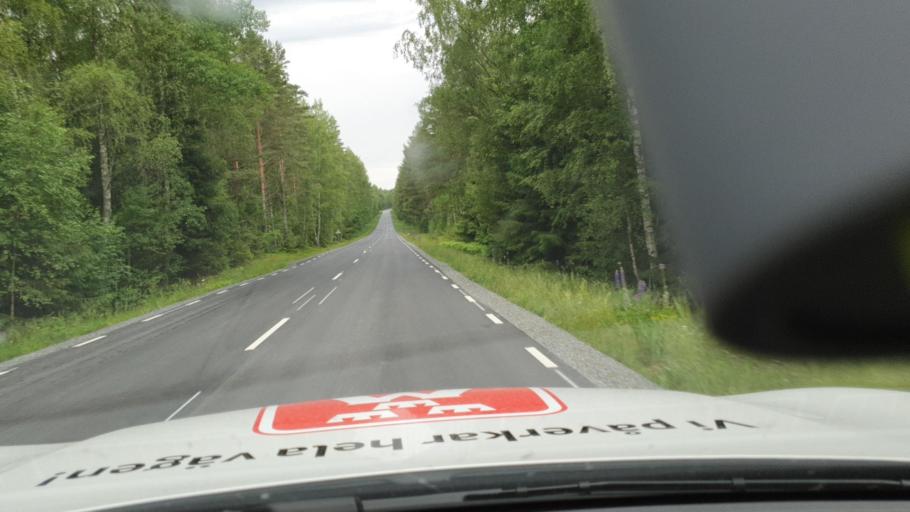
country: SE
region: Vaestra Goetaland
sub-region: Gullspangs Kommun
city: Anderstorp
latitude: 58.9210
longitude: 14.4331
